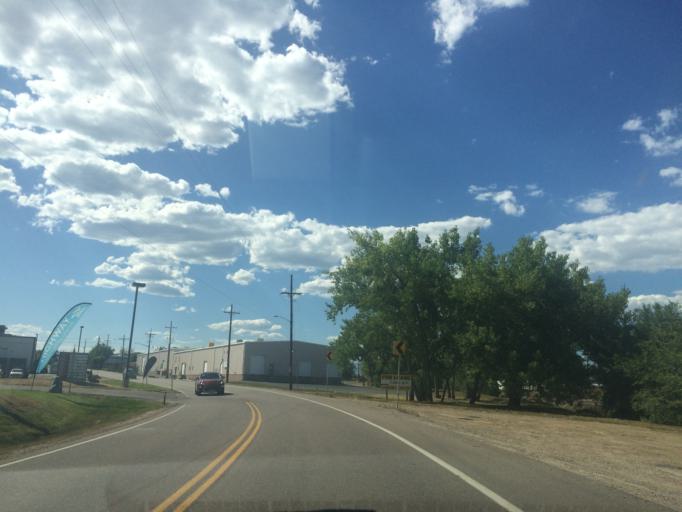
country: US
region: Colorado
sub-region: Broomfield County
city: Broomfield
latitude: 39.9213
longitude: -105.0972
